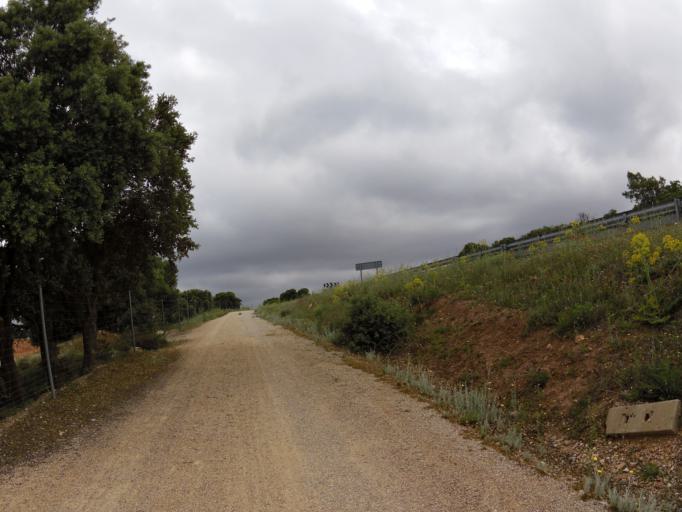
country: ES
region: Castille-La Mancha
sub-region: Provincia de Albacete
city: Robledo
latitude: 38.7342
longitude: -2.4670
